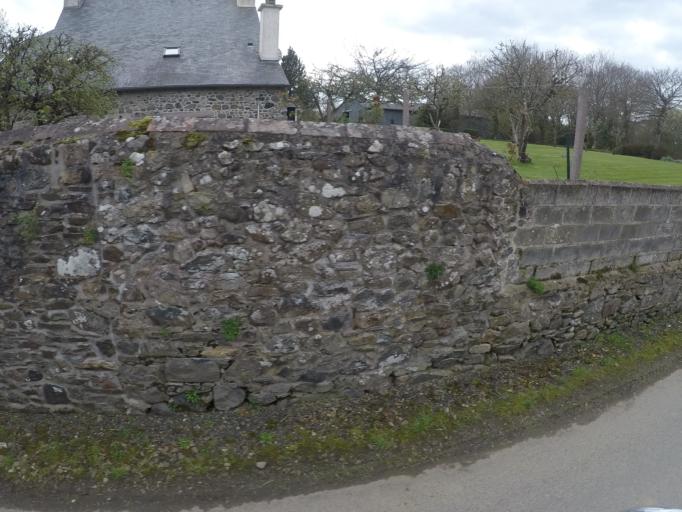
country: FR
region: Brittany
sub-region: Departement des Cotes-d'Armor
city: Plouha
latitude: 48.6561
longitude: -2.9193
